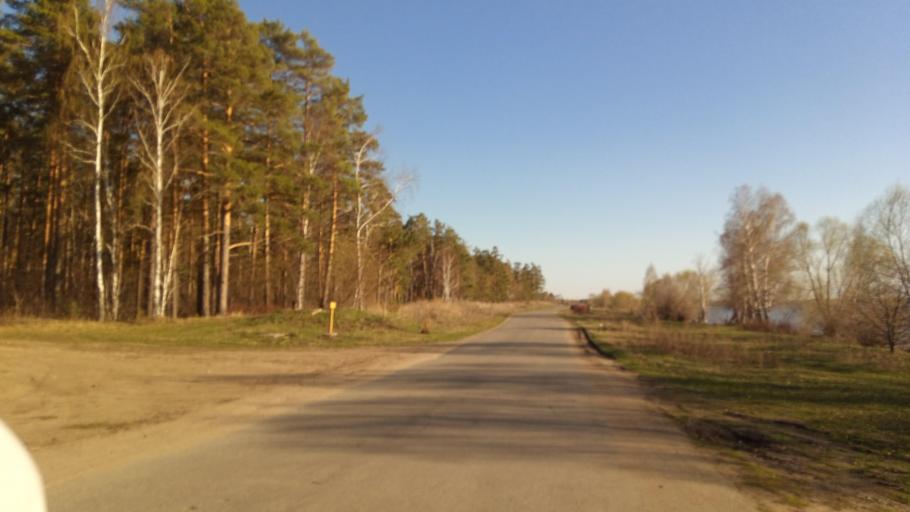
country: RU
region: Chelyabinsk
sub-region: Gorod Chelyabinsk
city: Chelyabinsk
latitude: 55.1314
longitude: 61.3280
